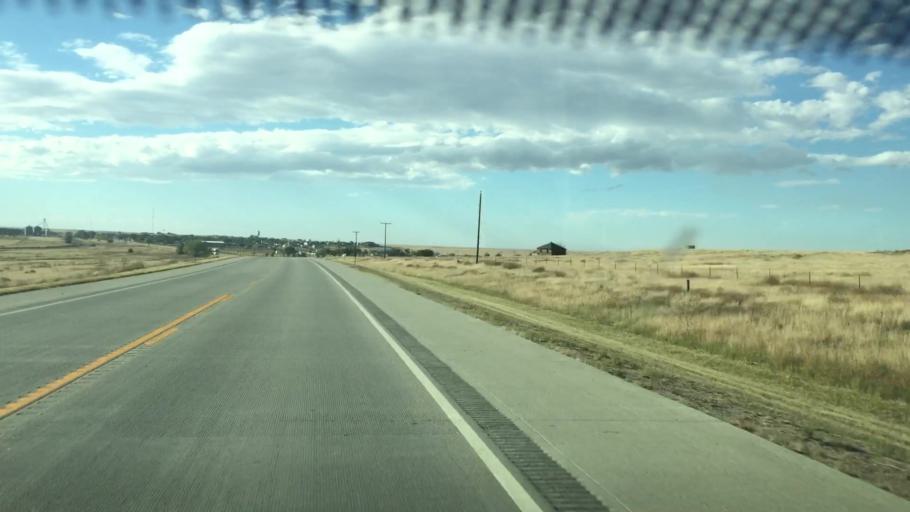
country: US
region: Colorado
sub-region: Lincoln County
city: Hugo
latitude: 39.1248
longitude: -103.4441
